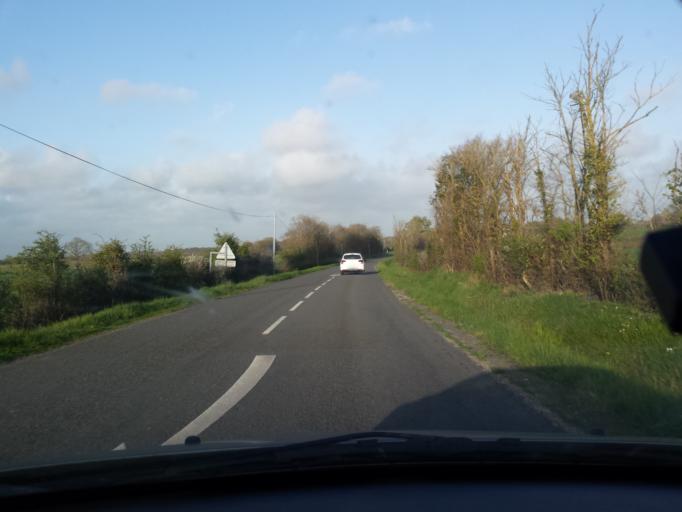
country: FR
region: Pays de la Loire
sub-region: Departement de la Vendee
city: Vaire
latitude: 46.5699
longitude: -1.7626
